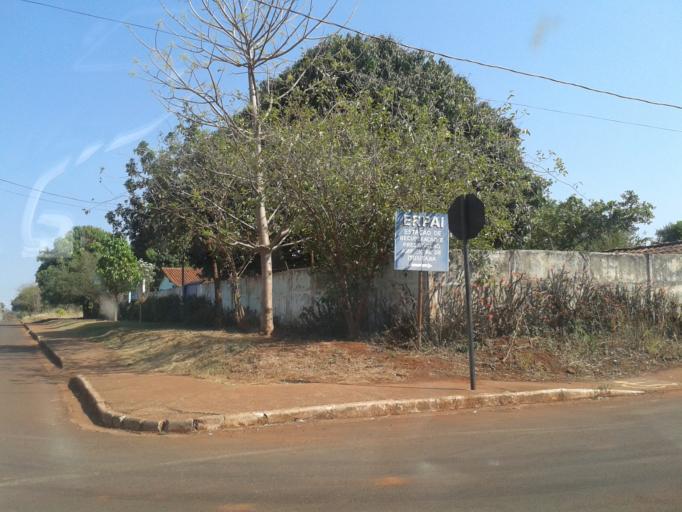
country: BR
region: Minas Gerais
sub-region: Ituiutaba
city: Ituiutaba
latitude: -18.9592
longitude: -49.4784
